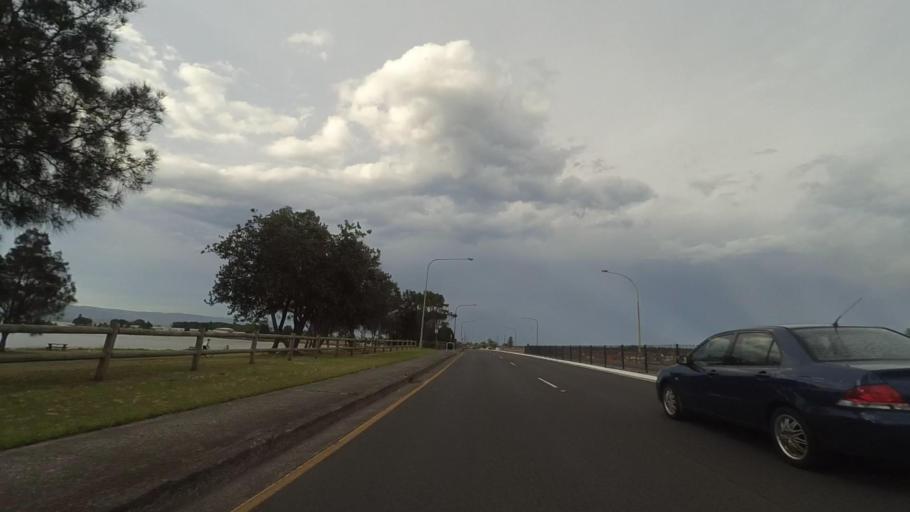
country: AU
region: New South Wales
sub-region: Shellharbour
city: Lake Illawarra
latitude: -34.5380
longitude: 150.8659
